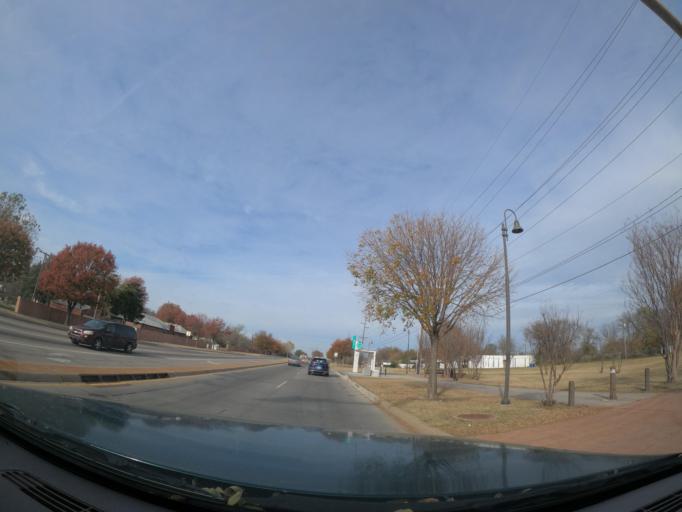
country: US
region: Oklahoma
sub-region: Tulsa County
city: Tulsa
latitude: 36.1917
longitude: -95.9758
